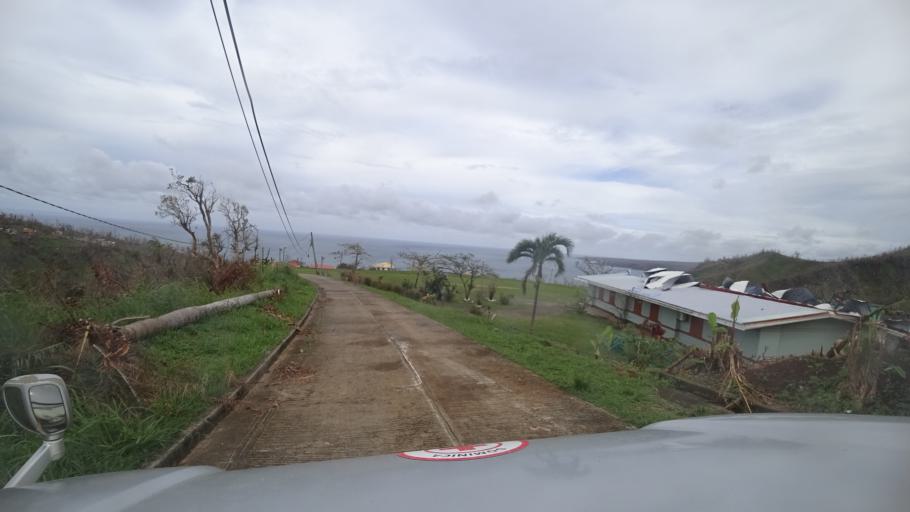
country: DM
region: Saint John
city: Portsmouth
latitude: 15.6132
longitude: -61.4114
